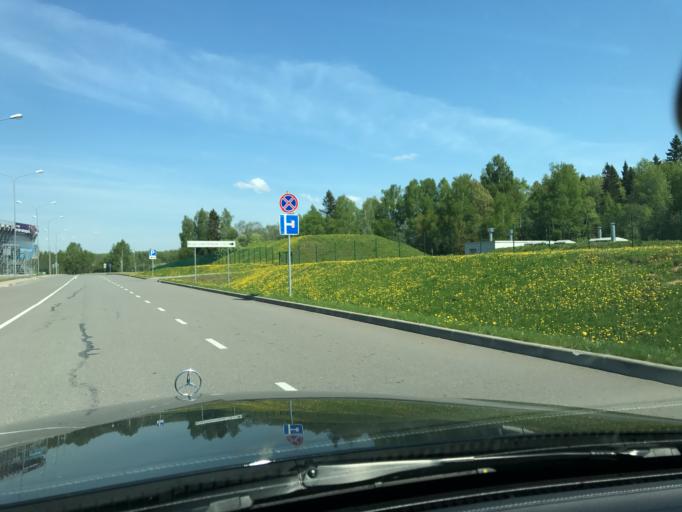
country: RU
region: Moskovskaya
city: Sychevo
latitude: 55.9961
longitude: 36.2723
